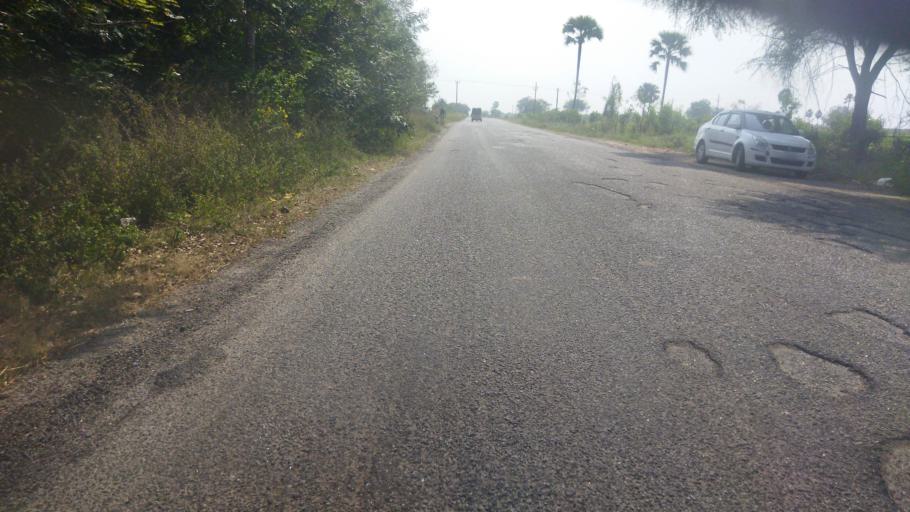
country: IN
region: Telangana
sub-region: Nalgonda
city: Nalgonda
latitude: 17.1026
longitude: 79.2829
